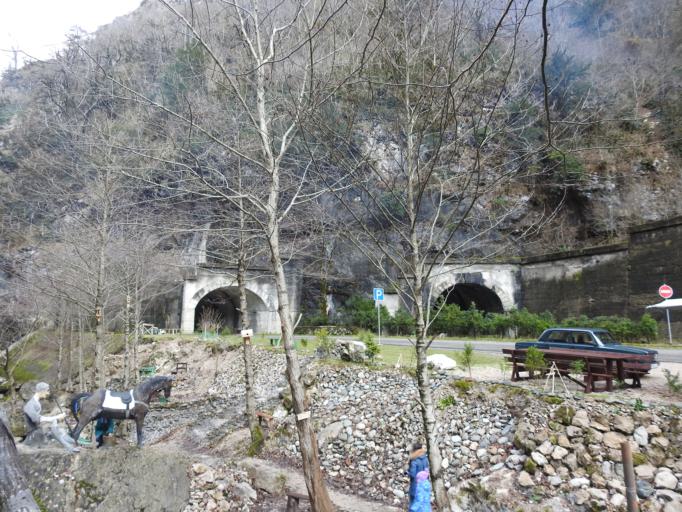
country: GE
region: Abkhazia
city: Gagra
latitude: 43.3750
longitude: 40.4625
